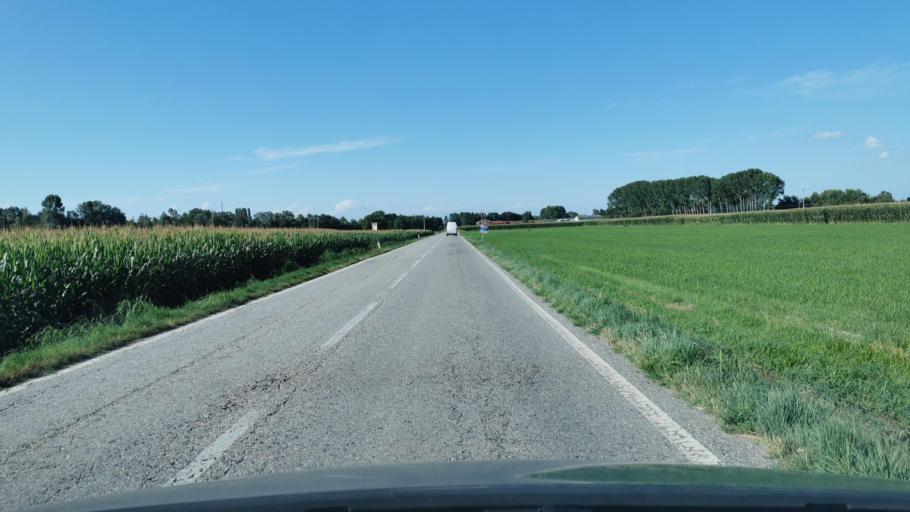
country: IT
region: Piedmont
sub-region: Provincia di Cuneo
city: Genola
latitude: 44.6020
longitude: 7.6218
